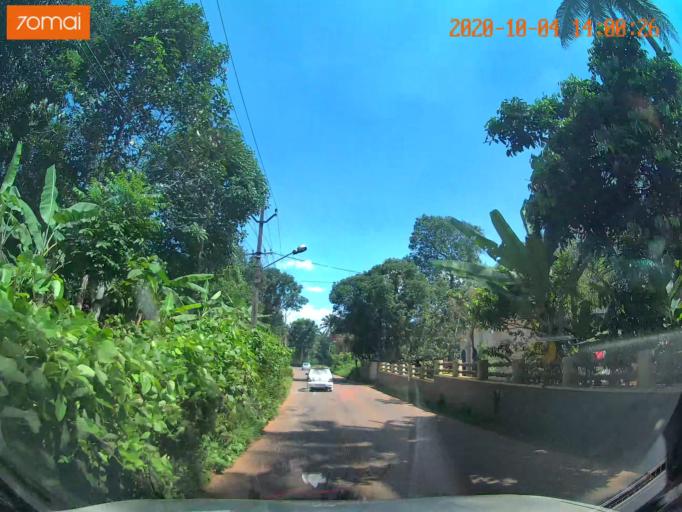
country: IN
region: Kerala
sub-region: Kottayam
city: Lalam
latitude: 9.7129
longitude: 76.6684
